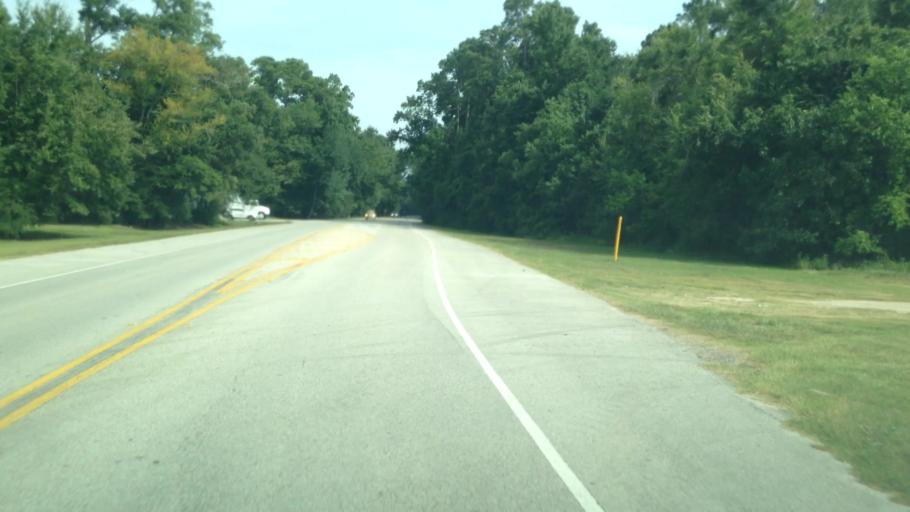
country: US
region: Texas
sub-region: Harris County
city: Sheldon
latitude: 29.9200
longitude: -95.1651
